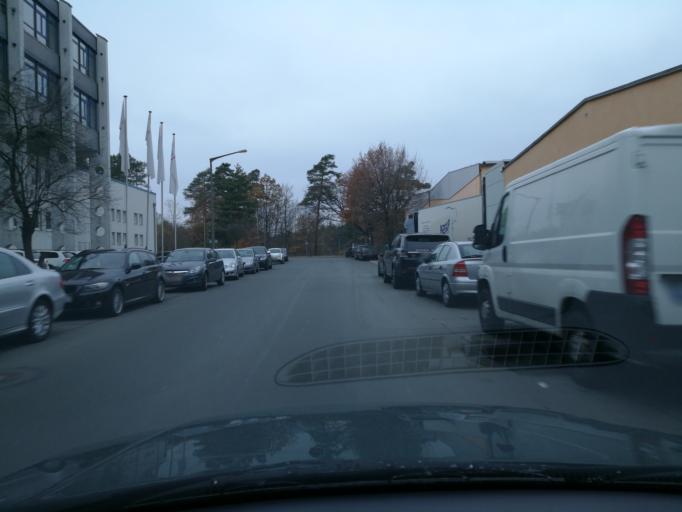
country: DE
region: Bavaria
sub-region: Regierungsbezirk Mittelfranken
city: Feucht
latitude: 49.4162
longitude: 11.1646
